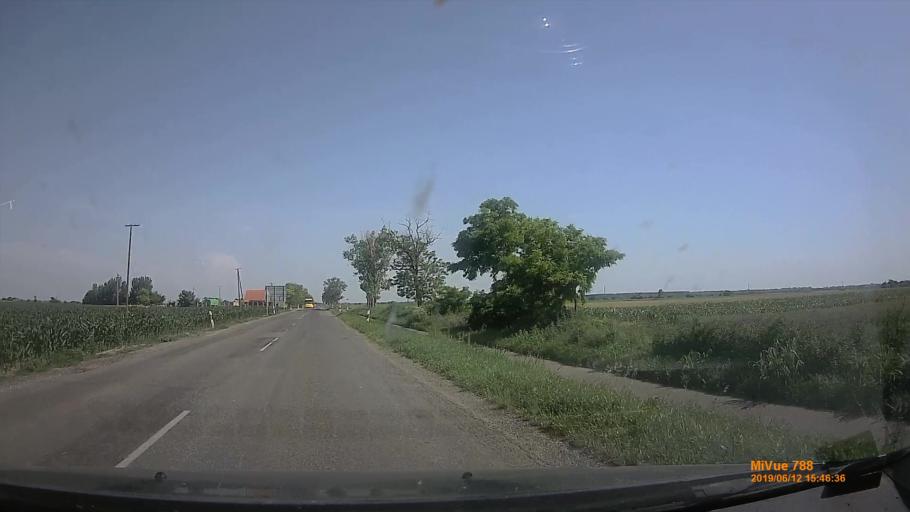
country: HU
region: Csongrad
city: Mako
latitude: 46.2150
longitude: 20.5221
